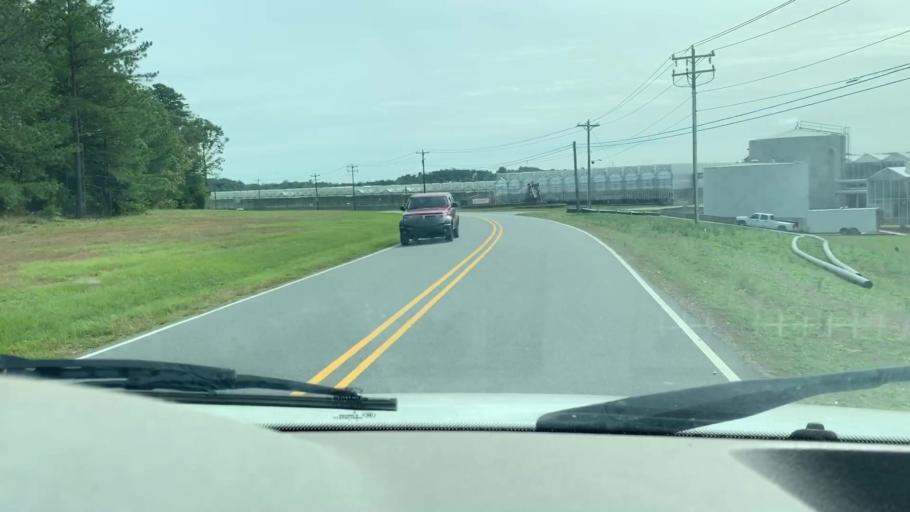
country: US
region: North Carolina
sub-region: Mecklenburg County
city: Huntersville
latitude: 35.4223
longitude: -80.7778
